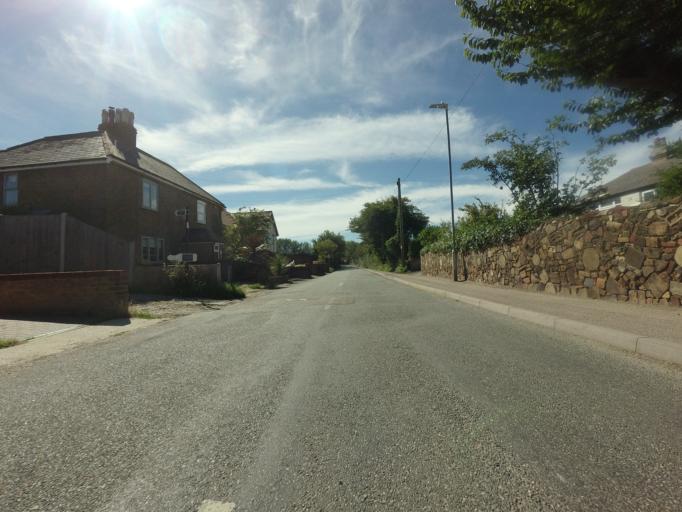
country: GB
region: England
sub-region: Kent
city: Birchington-on-Sea
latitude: 51.3358
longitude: 1.3019
